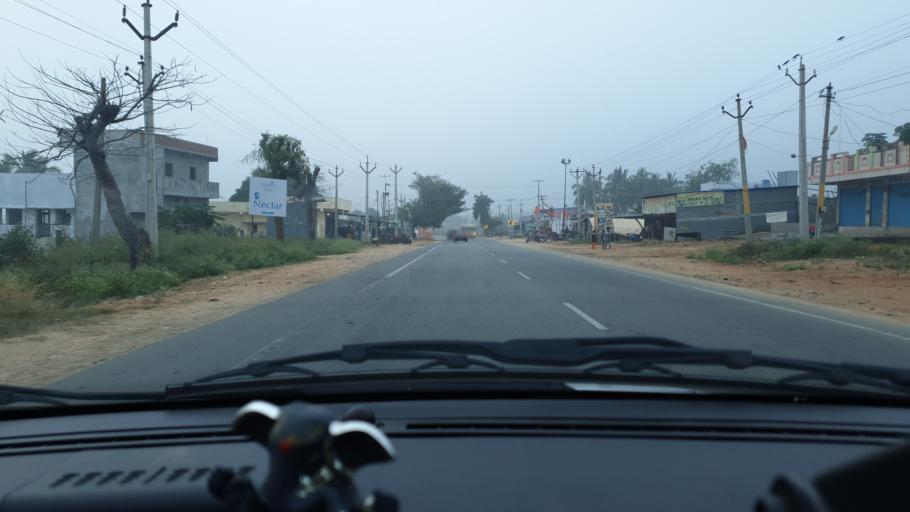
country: IN
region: Telangana
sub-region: Mahbubnagar
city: Farrukhnagar
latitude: 16.9266
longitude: 78.5275
